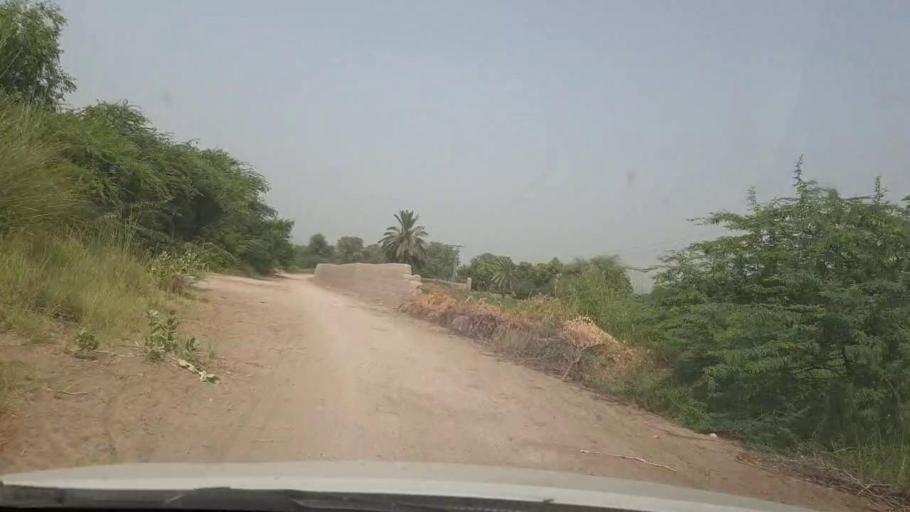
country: PK
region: Sindh
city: Kot Diji
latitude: 27.3066
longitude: 68.6869
